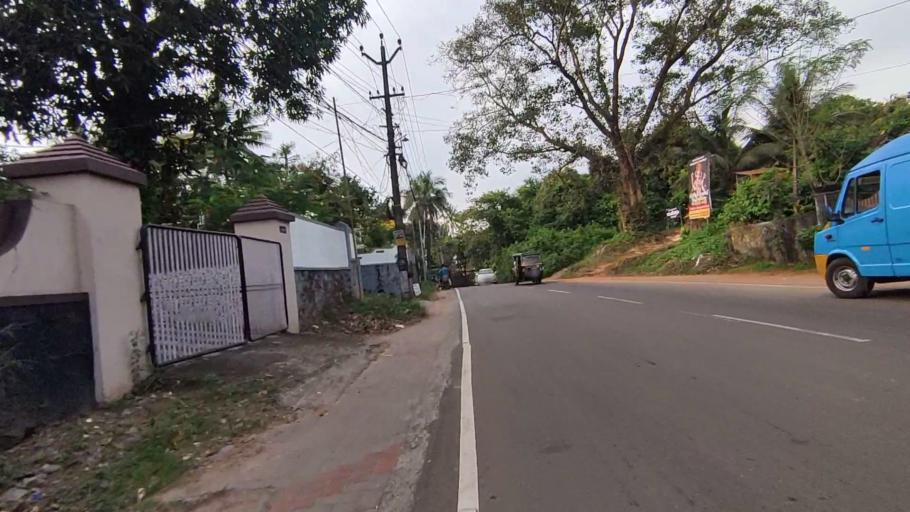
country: IN
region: Kerala
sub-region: Kottayam
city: Kottayam
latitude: 9.6219
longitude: 76.5113
